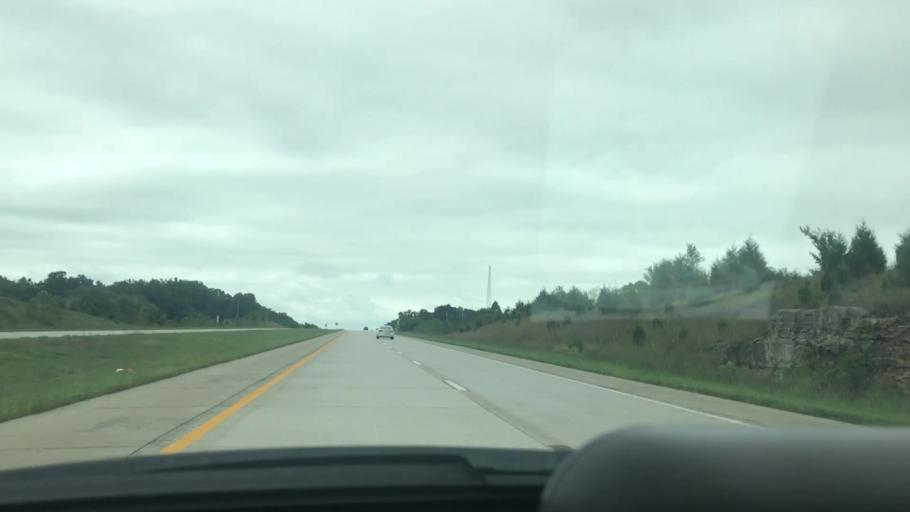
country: US
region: Missouri
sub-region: Dallas County
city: Buffalo
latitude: 37.5363
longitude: -93.1373
